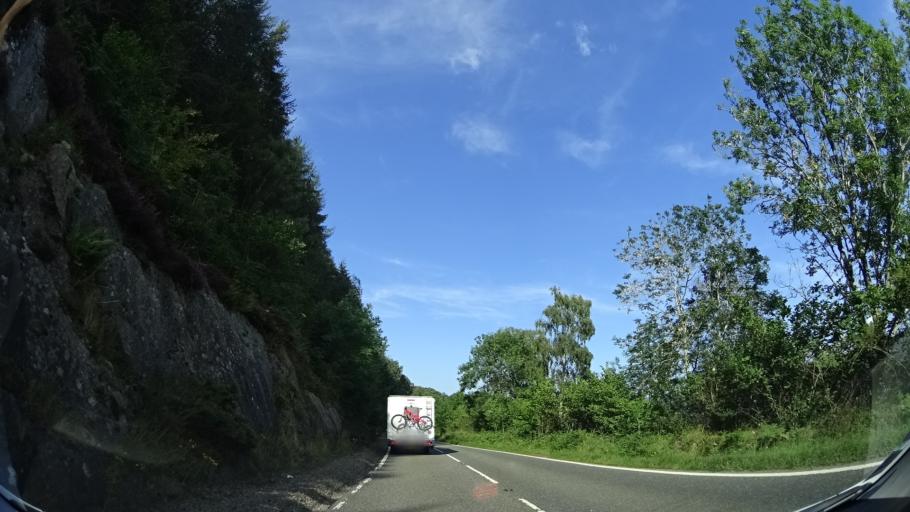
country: GB
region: Scotland
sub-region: Highland
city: Beauly
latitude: 57.3587
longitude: -4.3993
